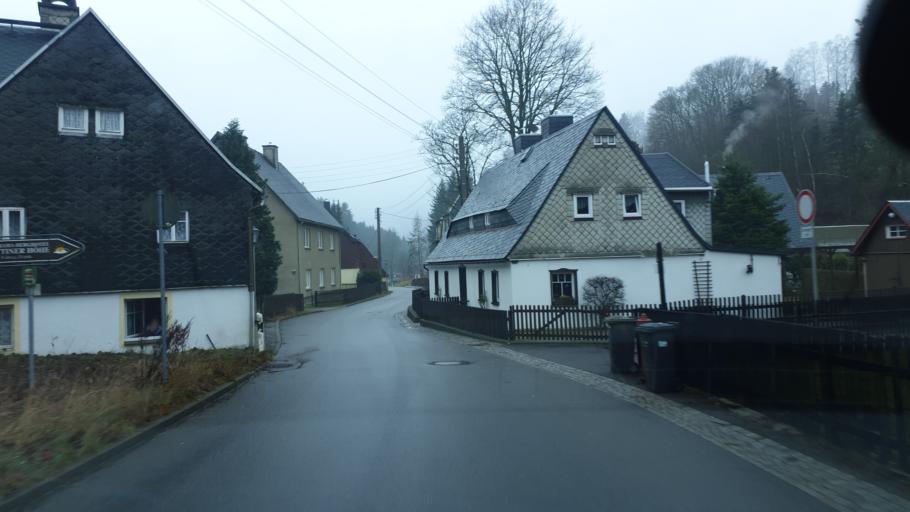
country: DE
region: Saxony
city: Seiffen
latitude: 50.6481
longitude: 13.4423
